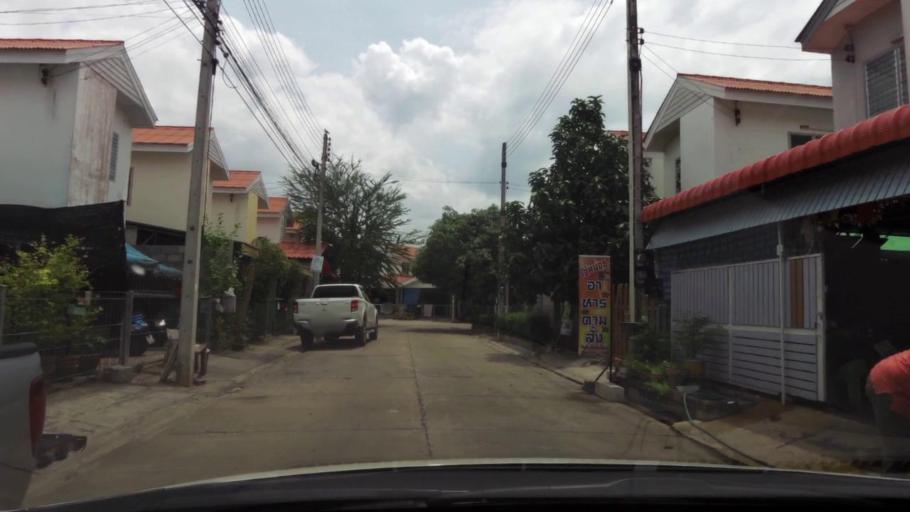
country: TH
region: Ratchaburi
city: Ratchaburi
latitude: 13.5378
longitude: 99.7935
